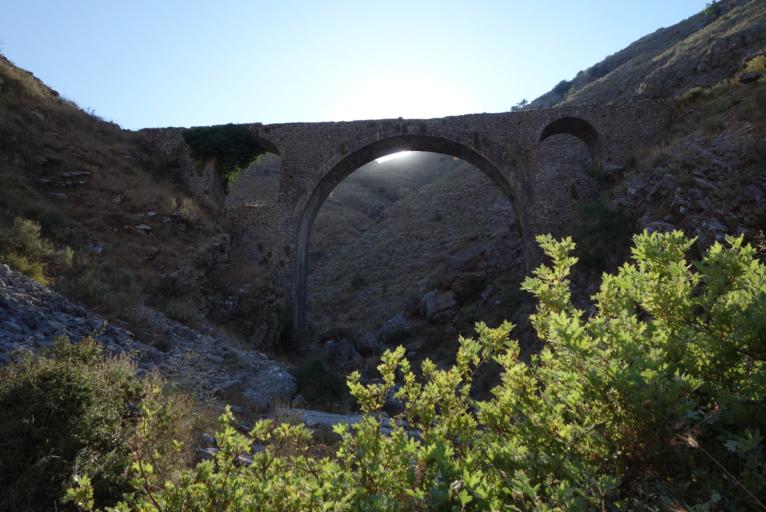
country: AL
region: Gjirokaster
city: Gjirokaster
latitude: 40.0647
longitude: 20.1322
